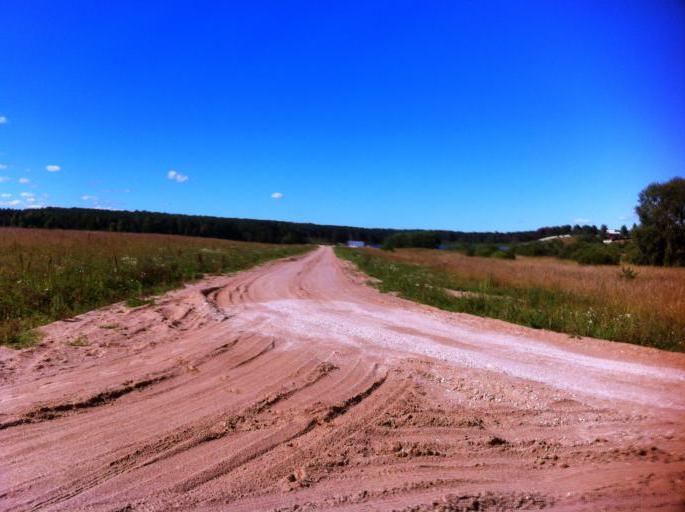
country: RU
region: Pskov
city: Izborsk
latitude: 57.8210
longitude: 27.9637
